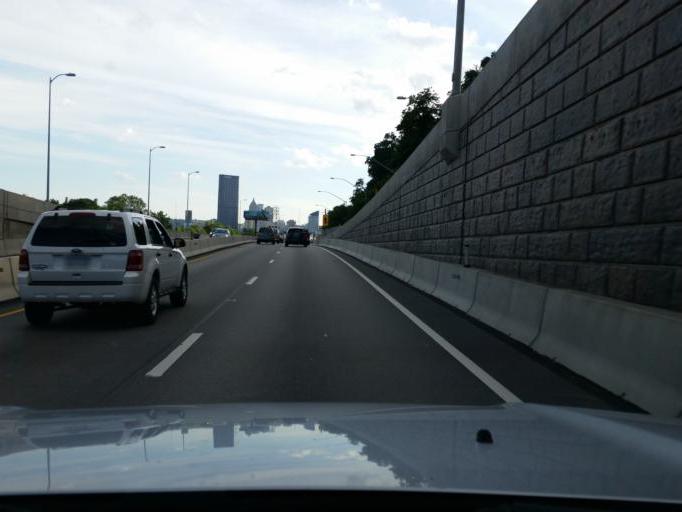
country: US
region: Pennsylvania
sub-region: Allegheny County
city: Millvale
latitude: 40.4643
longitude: -79.9802
